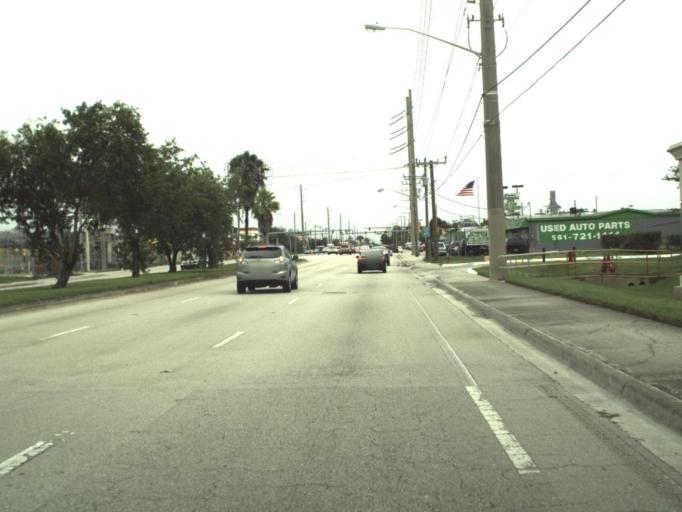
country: US
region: Florida
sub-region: Palm Beach County
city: Lake Worth Corridor
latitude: 26.6158
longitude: -80.1135
